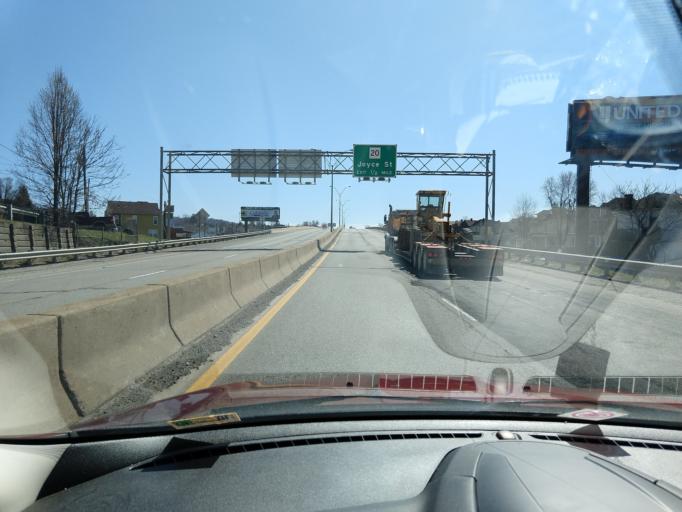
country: US
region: West Virginia
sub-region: Harrison County
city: Clarksburg
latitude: 39.2787
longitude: -80.3284
